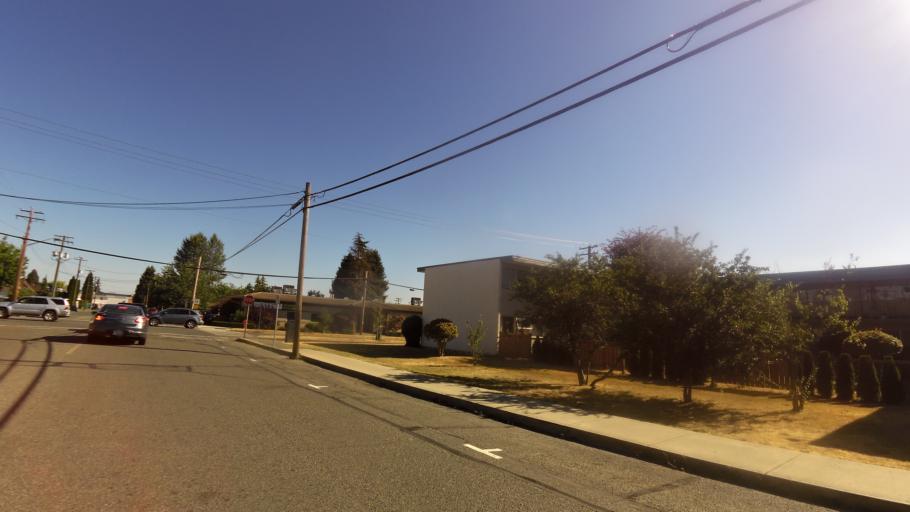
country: CA
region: British Columbia
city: Duncan
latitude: 48.7783
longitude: -123.7020
